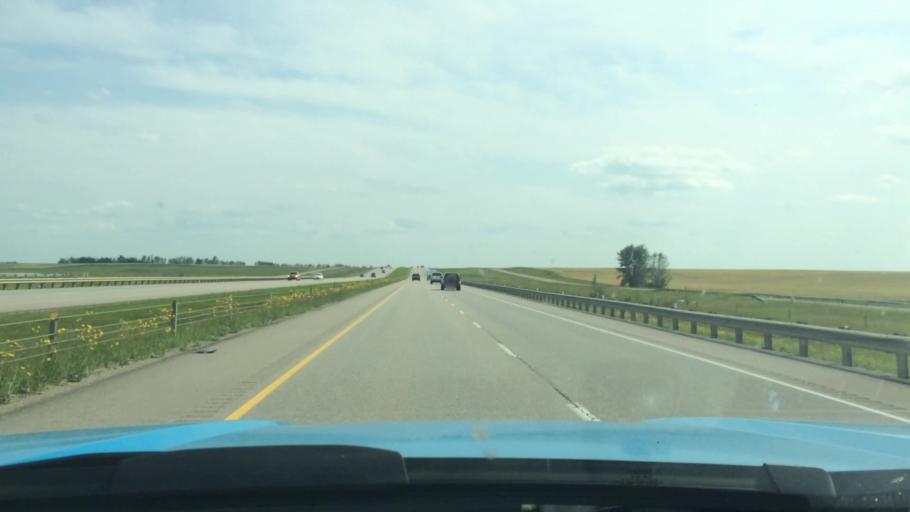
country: CA
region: Alberta
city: Carstairs
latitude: 51.6365
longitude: -114.0256
